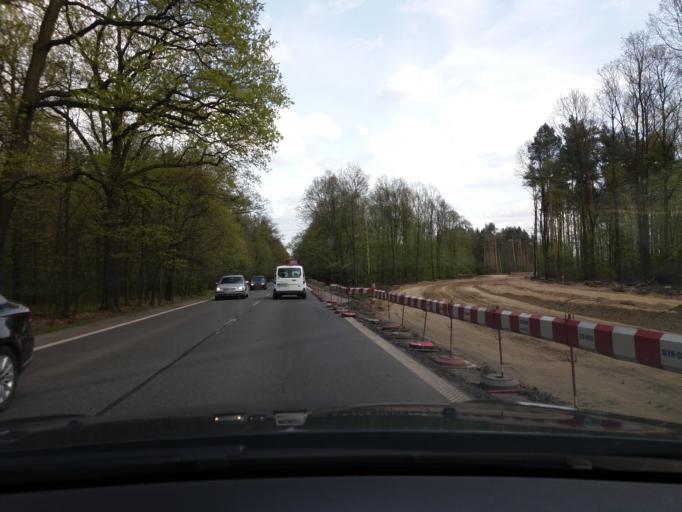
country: PL
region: Lower Silesian Voivodeship
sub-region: Powiat sredzki
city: Mrozow
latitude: 51.1491
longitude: 16.8392
